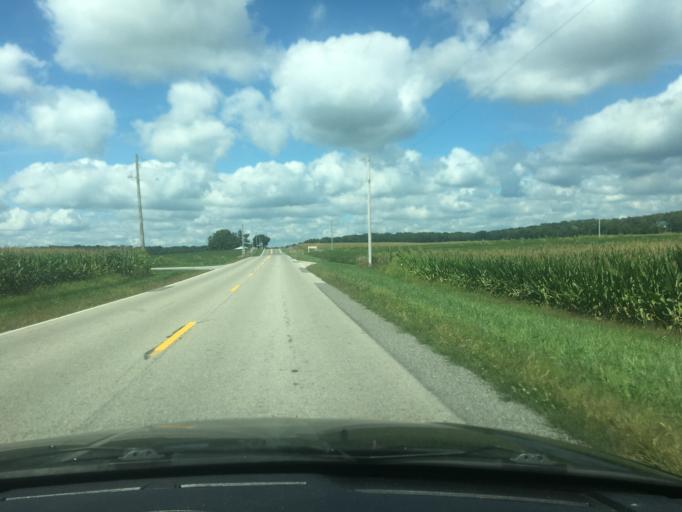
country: US
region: Ohio
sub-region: Logan County
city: West Liberty
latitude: 40.2389
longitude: -83.7112
